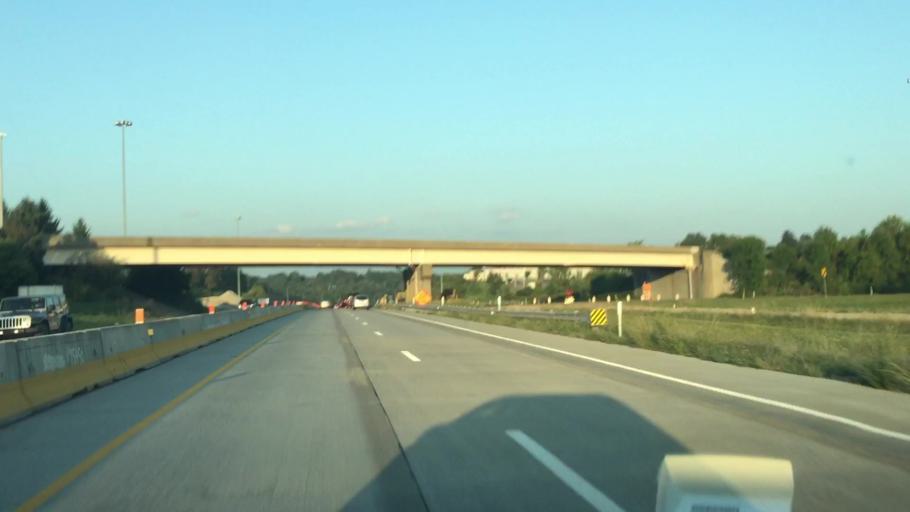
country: US
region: Pennsylvania
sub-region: Allegheny County
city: Enlow
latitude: 40.4721
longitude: -80.2244
